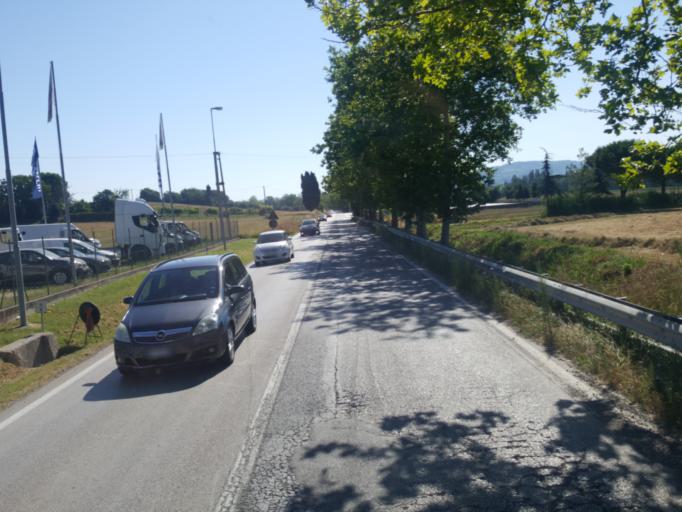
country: IT
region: The Marches
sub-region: Provincia di Pesaro e Urbino
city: Borgo Santa Maria
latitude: 43.8750
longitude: 12.8065
